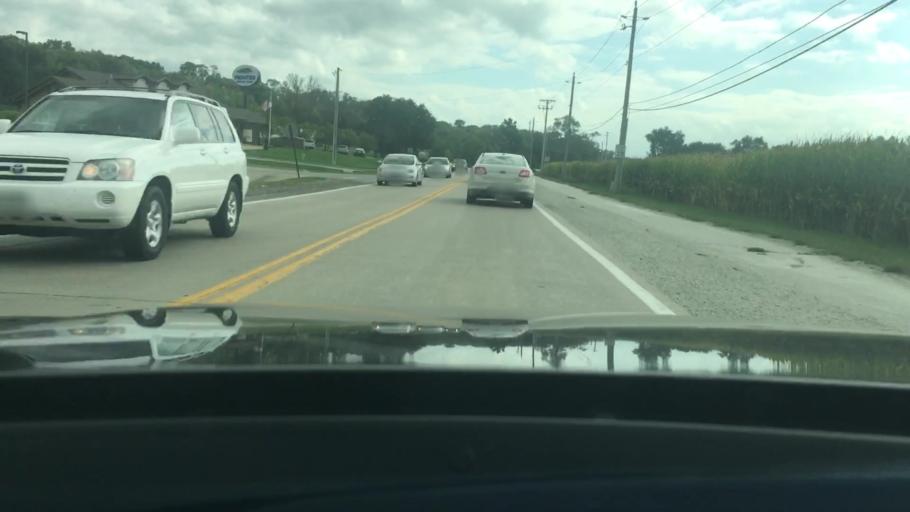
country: US
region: Iowa
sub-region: Pottawattamie County
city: Council Bluffs
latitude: 41.2498
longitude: -95.8144
